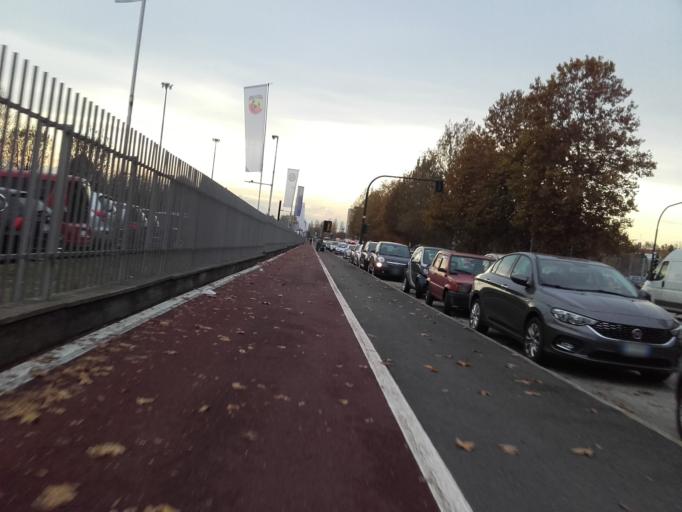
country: IT
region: Piedmont
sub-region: Provincia di Torino
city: Turin
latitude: 45.1104
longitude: 7.7105
